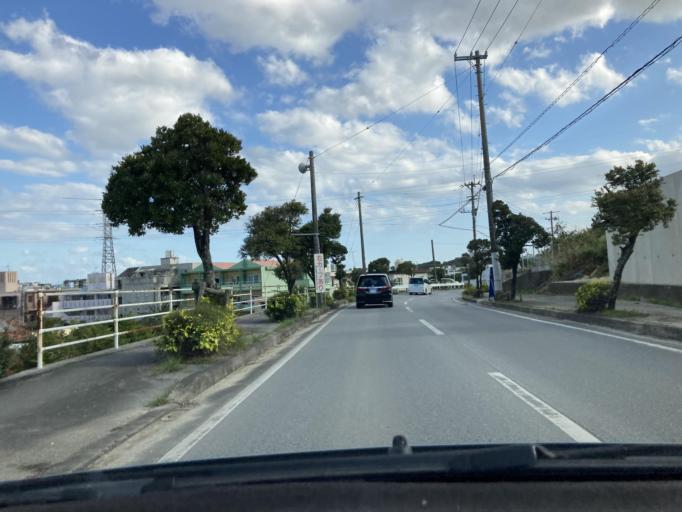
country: JP
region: Okinawa
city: Tomigusuku
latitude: 26.1876
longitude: 127.7070
